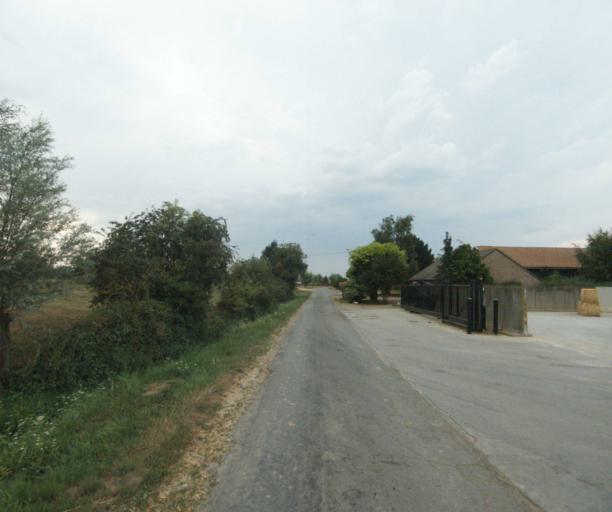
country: FR
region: Nord-Pas-de-Calais
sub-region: Departement du Nord
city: Comines
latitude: 50.7477
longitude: 2.9867
